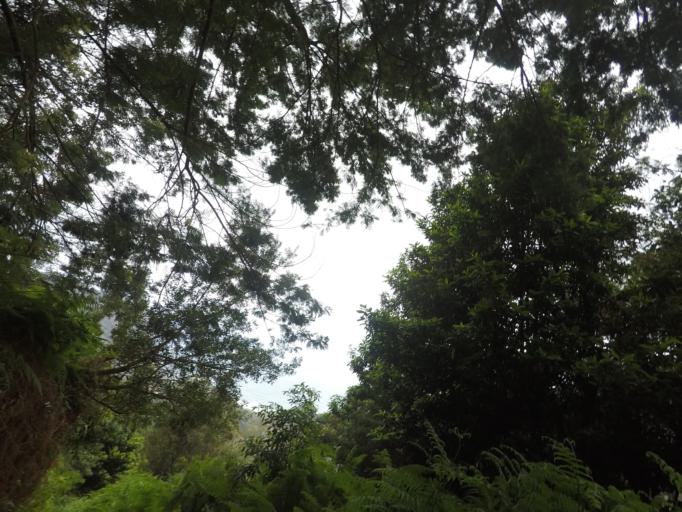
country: PT
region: Madeira
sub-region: Santa Cruz
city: Santa Cruz
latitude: 32.7496
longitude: -16.8249
